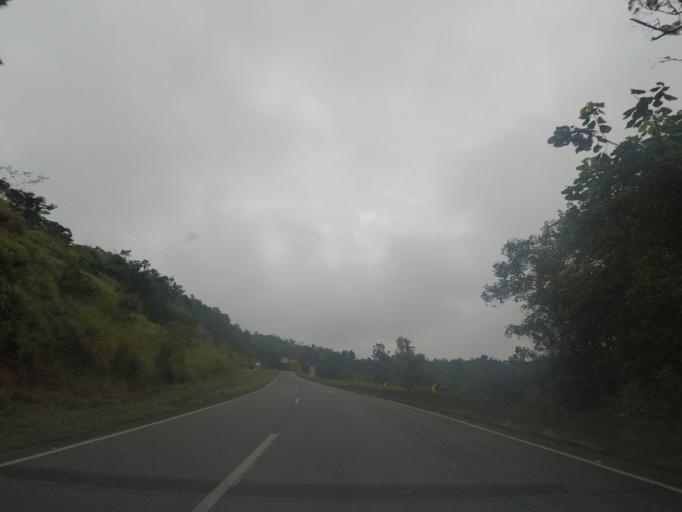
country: BR
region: Parana
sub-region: Antonina
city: Antonina
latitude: -25.0605
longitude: -48.5632
